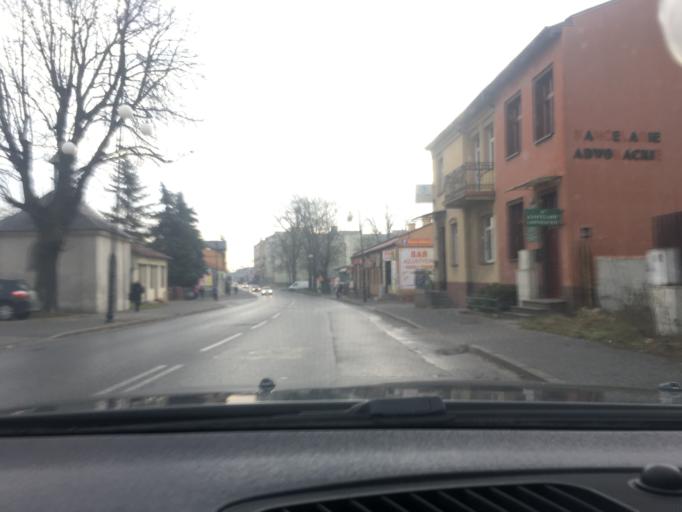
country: PL
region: Swietokrzyskie
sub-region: Powiat jedrzejowski
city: Jedrzejow
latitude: 50.6432
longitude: 20.2973
